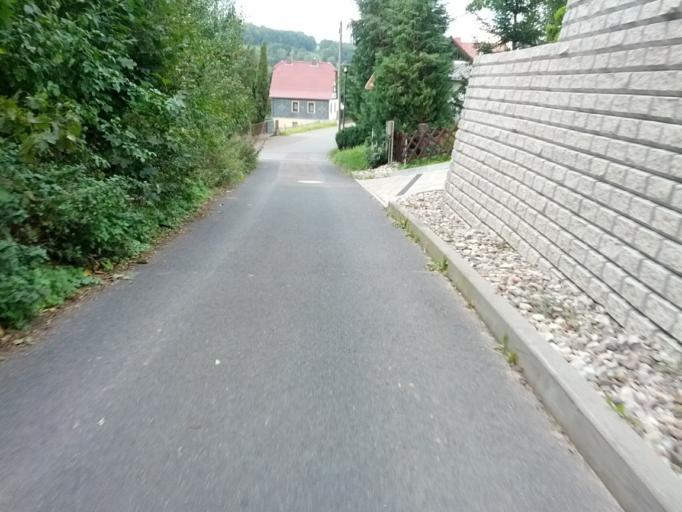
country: DE
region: Thuringia
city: Thal
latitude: 50.9342
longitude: 10.3960
